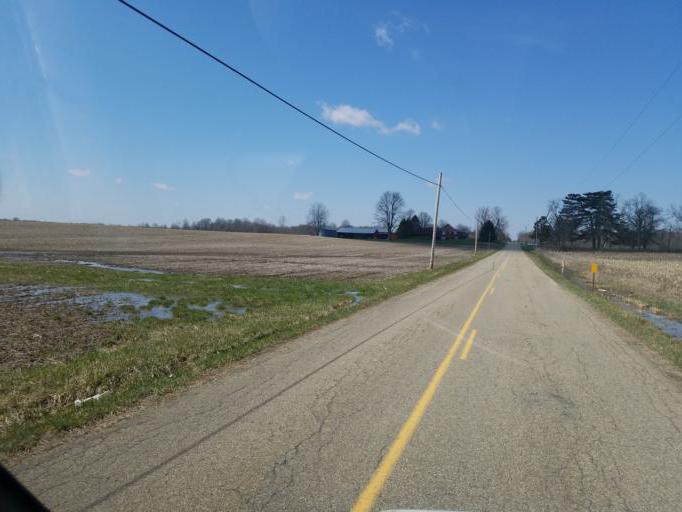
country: US
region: Ohio
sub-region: Knox County
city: Centerburg
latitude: 40.2958
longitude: -82.6726
